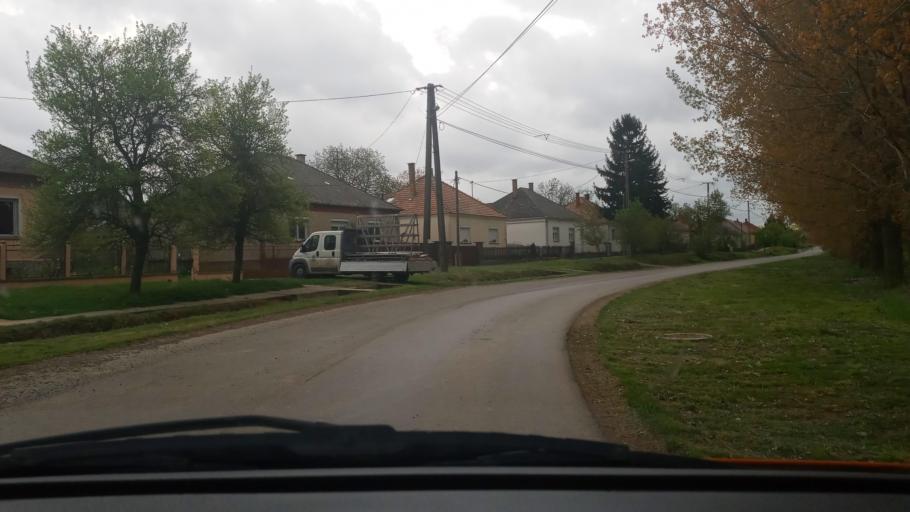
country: HU
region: Baranya
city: Boly
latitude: 45.9927
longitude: 18.5166
